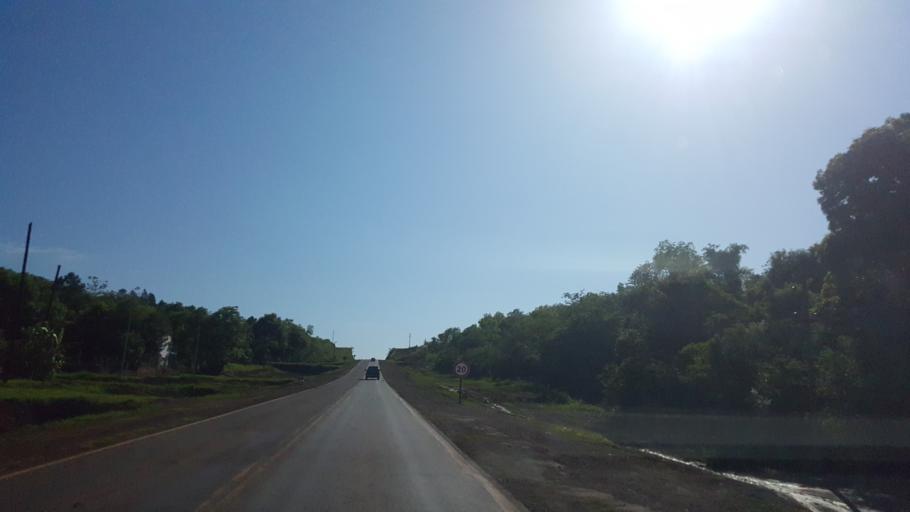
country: AR
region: Misiones
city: Santa Ana
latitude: -27.3731
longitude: -55.5695
